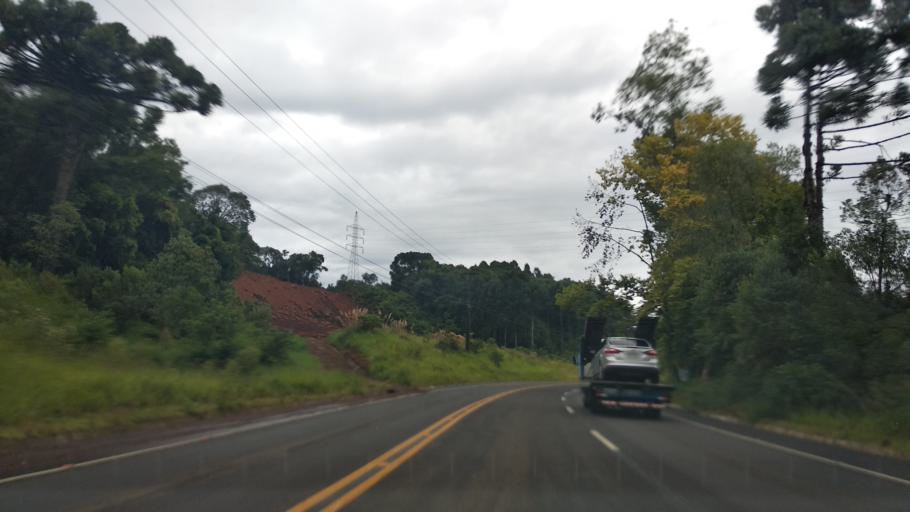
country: BR
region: Santa Catarina
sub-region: Videira
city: Videira
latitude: -27.0521
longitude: -51.1767
